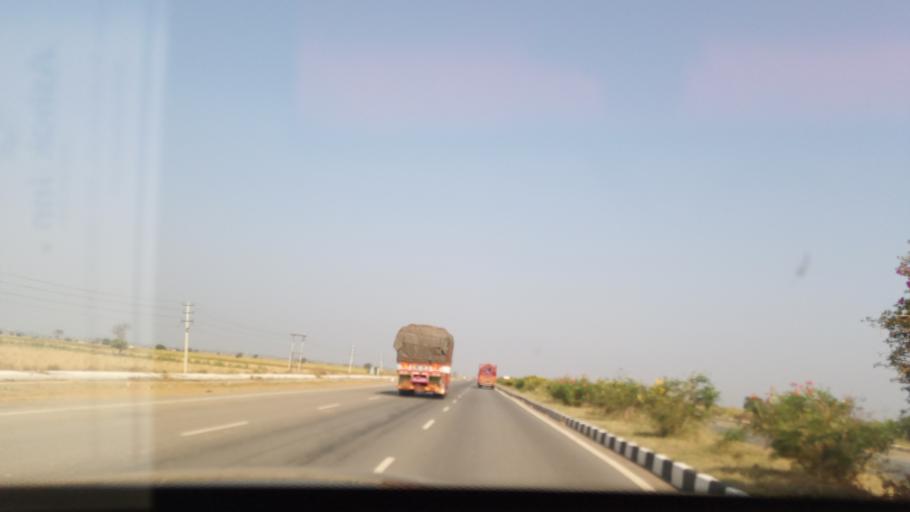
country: IN
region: Karnataka
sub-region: Haveri
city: Savanur
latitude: 14.8892
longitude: 75.3010
